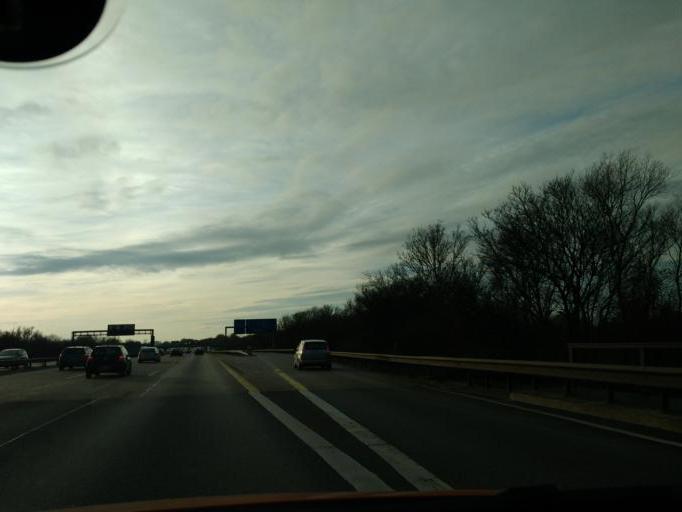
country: DE
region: Bremen
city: Bremen
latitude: 53.0320
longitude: 8.8654
